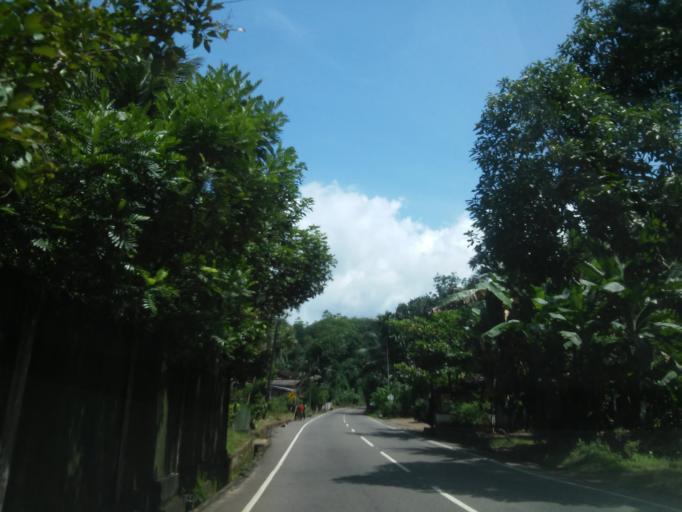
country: LK
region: Sabaragamuwa
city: Ratnapura
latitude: 6.7287
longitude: 80.3199
